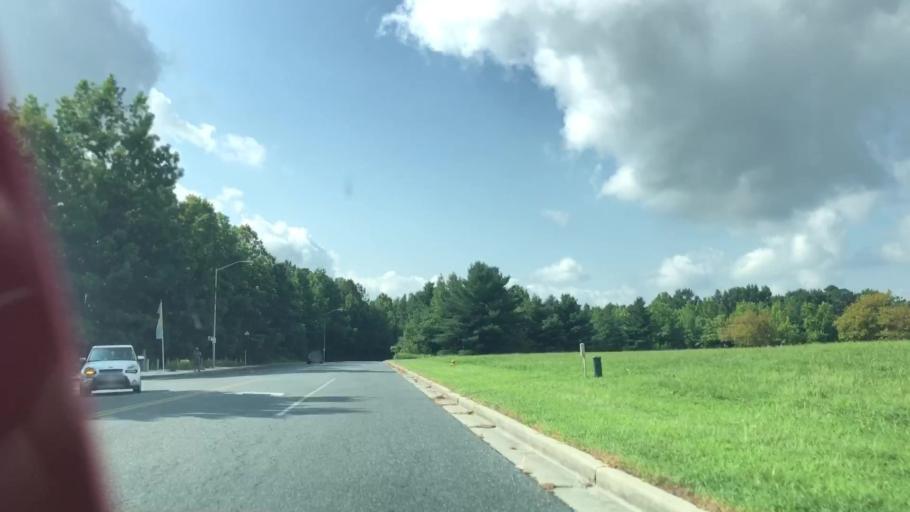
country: US
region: Maryland
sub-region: Wicomico County
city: Salisbury
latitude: 38.3979
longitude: -75.5628
